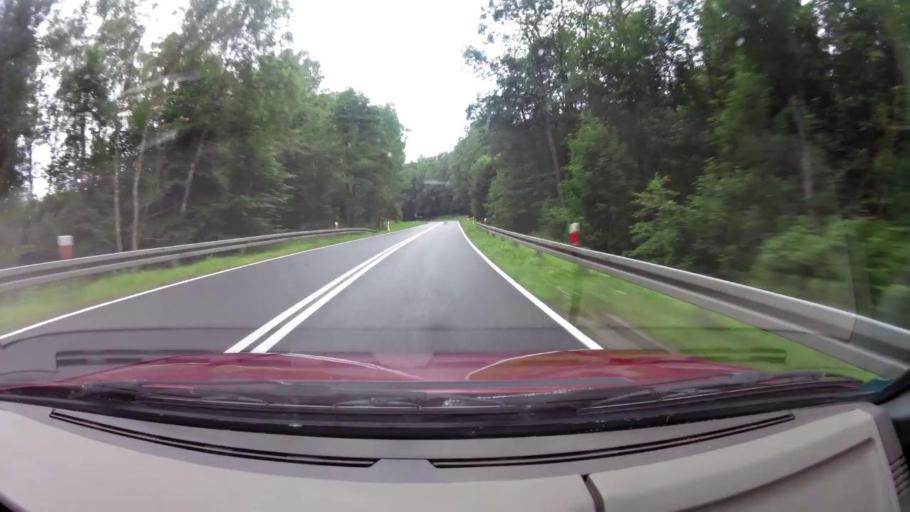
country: PL
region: West Pomeranian Voivodeship
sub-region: Powiat stargardzki
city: Chociwel
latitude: 53.5006
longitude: 15.4418
